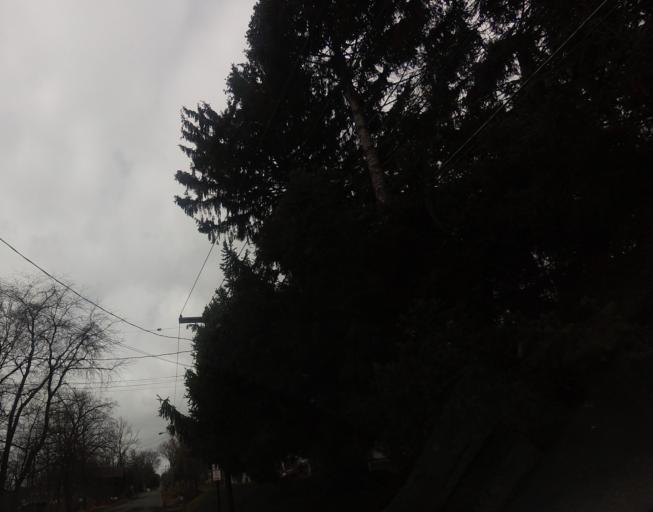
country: US
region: New York
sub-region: Tompkins County
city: Ithaca
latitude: 42.4363
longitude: -76.5234
